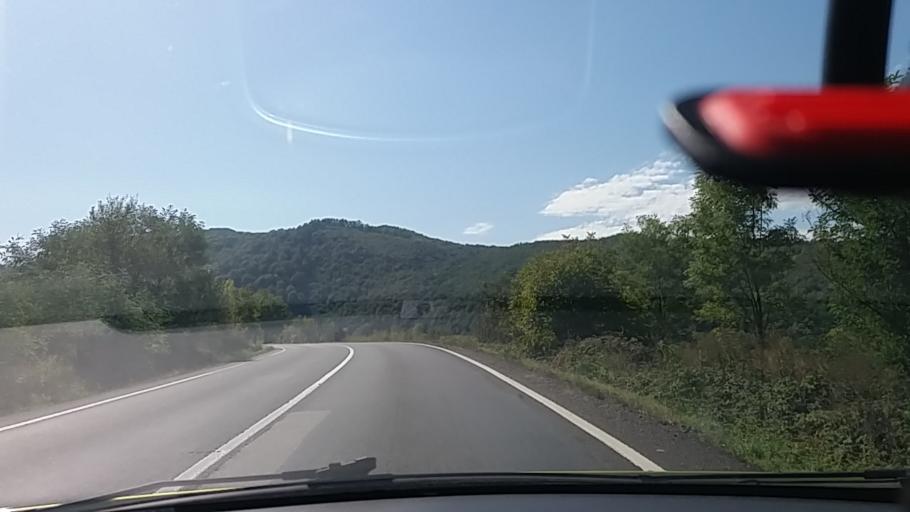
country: RO
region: Hunedoara
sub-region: Comuna Zam
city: Zam
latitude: 45.9836
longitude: 22.4308
